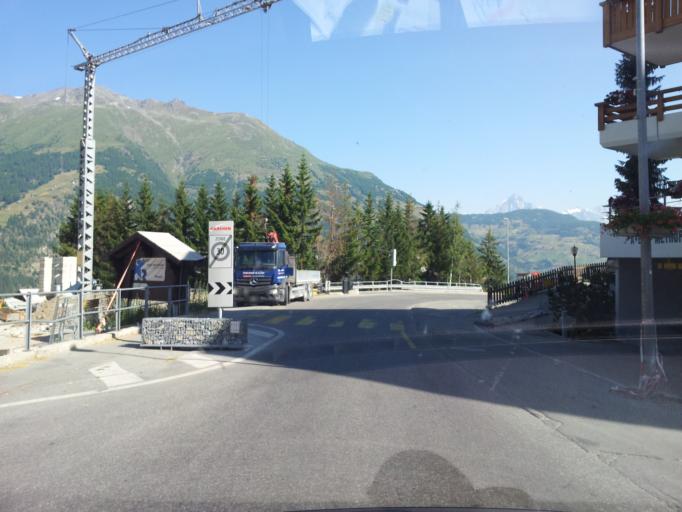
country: CH
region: Valais
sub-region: Visp District
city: Grachen
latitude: 46.1966
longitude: 7.8396
